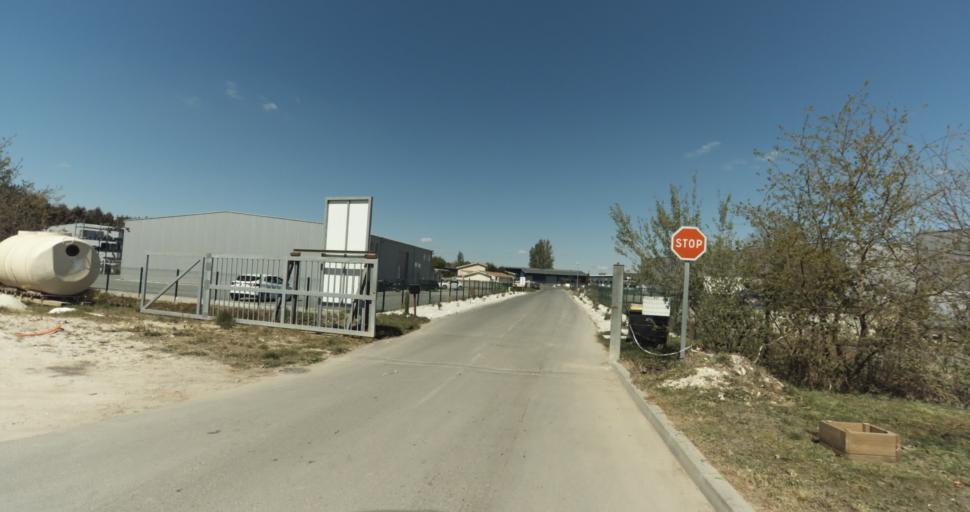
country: FR
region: Aquitaine
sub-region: Departement de la Gironde
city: Martignas-sur-Jalle
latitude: 44.8059
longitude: -0.7503
